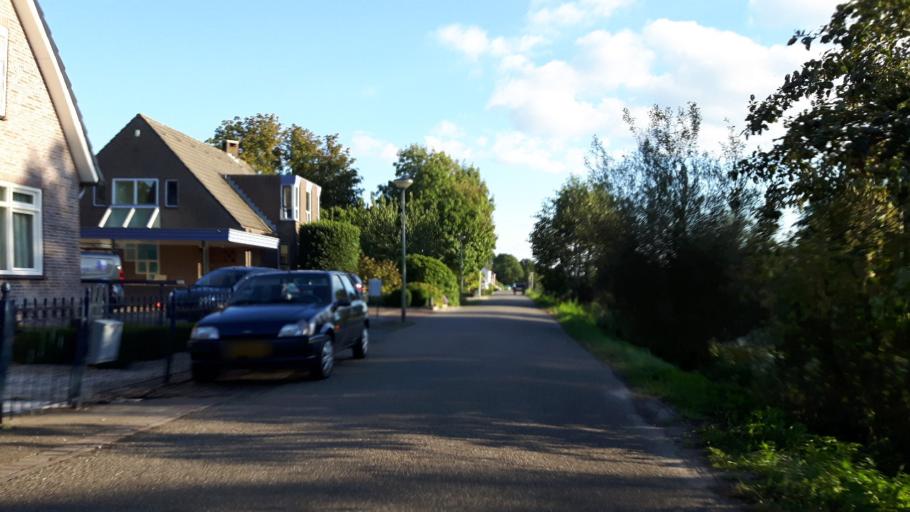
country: NL
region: Utrecht
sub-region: Gemeente Oudewater
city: Oudewater
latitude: 52.0338
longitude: 4.8617
